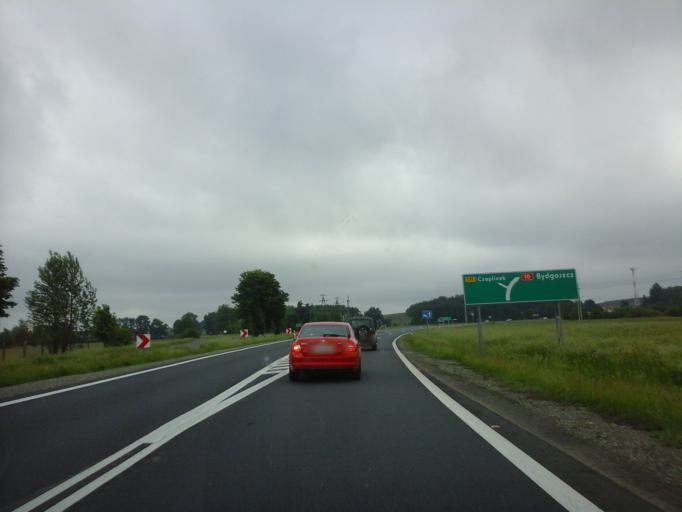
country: PL
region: West Pomeranian Voivodeship
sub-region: Powiat walecki
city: Miroslawiec
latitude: 53.3471
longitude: 16.1009
